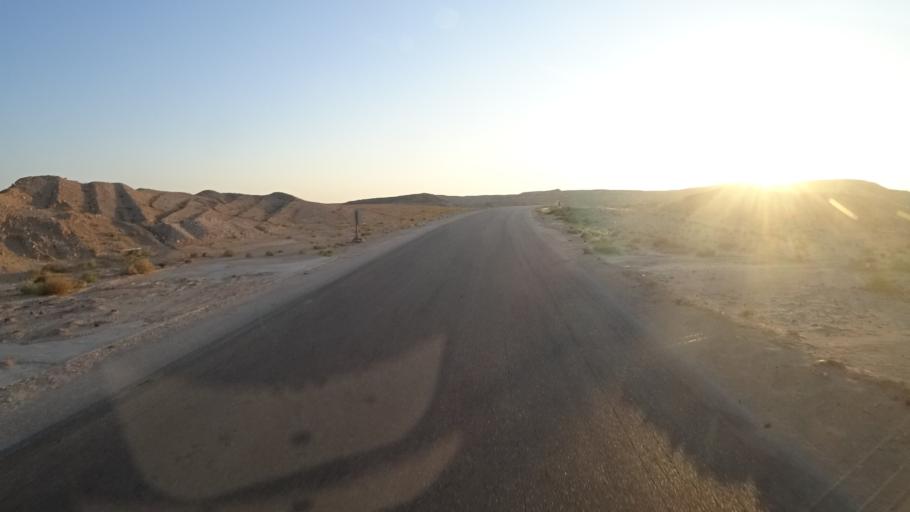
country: OM
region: Zufar
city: Salalah
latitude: 17.5114
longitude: 53.3704
